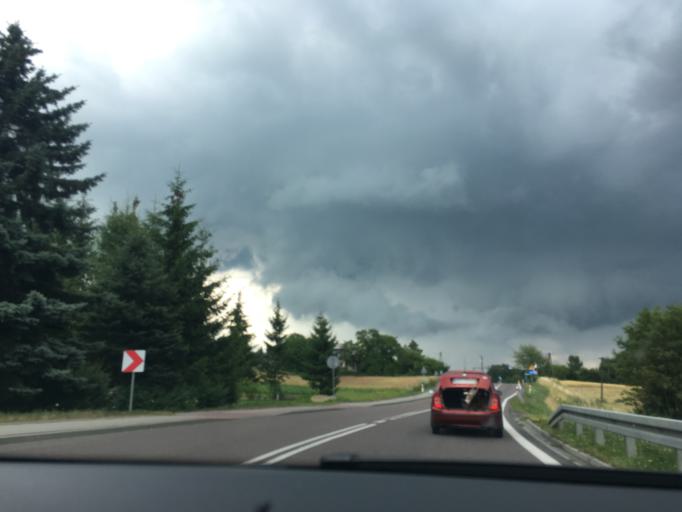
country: PL
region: Subcarpathian Voivodeship
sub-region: Powiat brzozowski
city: Jablonica Polska
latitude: 49.7229
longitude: 21.9018
